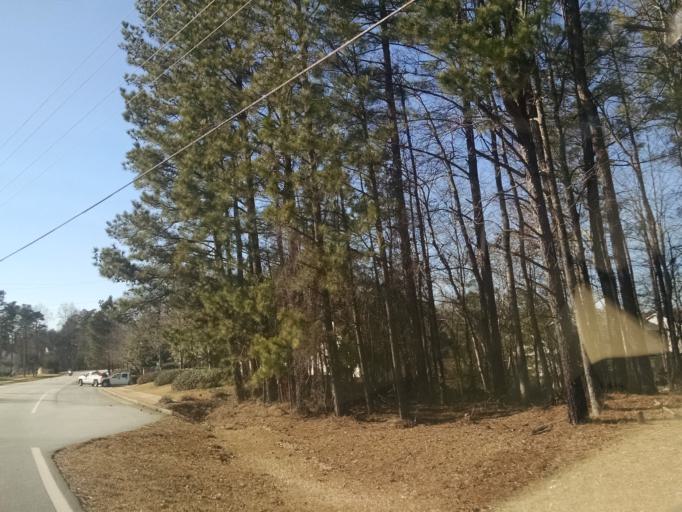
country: US
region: Georgia
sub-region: Gwinnett County
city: Sugar Hill
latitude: 34.1013
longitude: -84.0602
